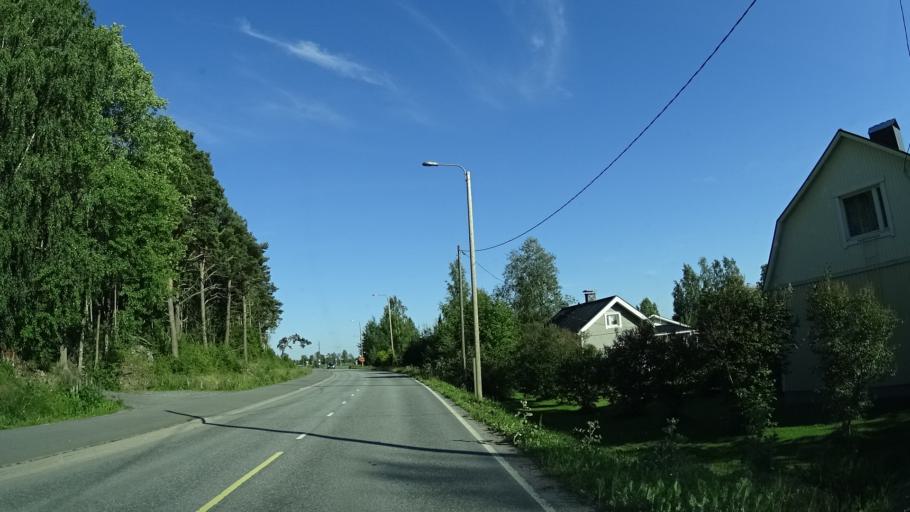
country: FI
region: Satakunta
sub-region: Pori
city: Ulvila
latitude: 61.5011
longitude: 21.8883
